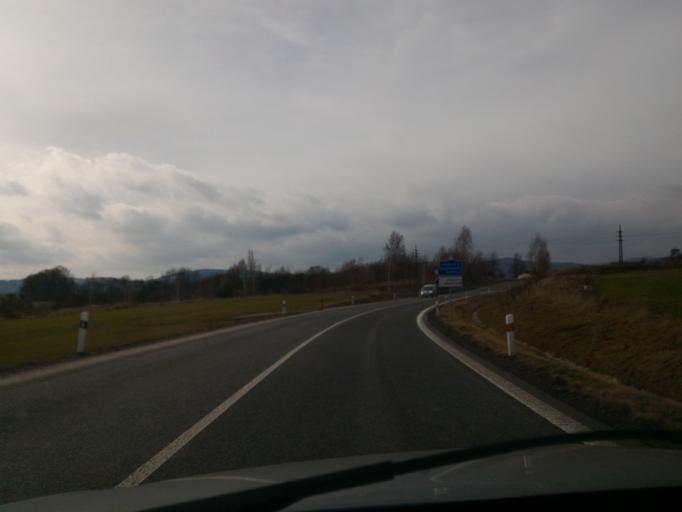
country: CZ
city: Hradek nad Nisou
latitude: 50.8528
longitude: 14.8692
